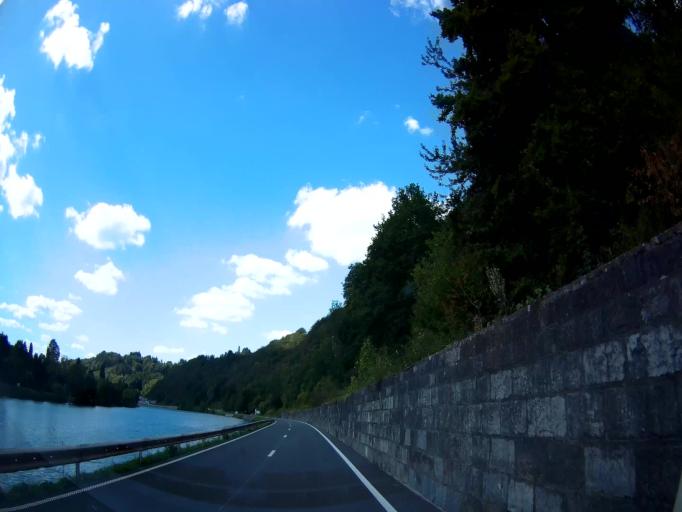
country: BE
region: Wallonia
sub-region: Province de Namur
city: Hastiere-Lavaux
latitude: 50.2157
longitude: 4.8409
